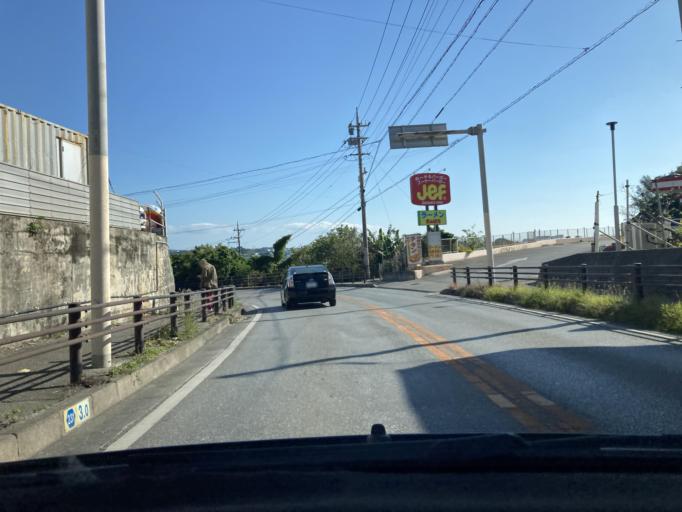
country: JP
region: Okinawa
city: Tomigusuku
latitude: 26.1818
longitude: 127.6623
